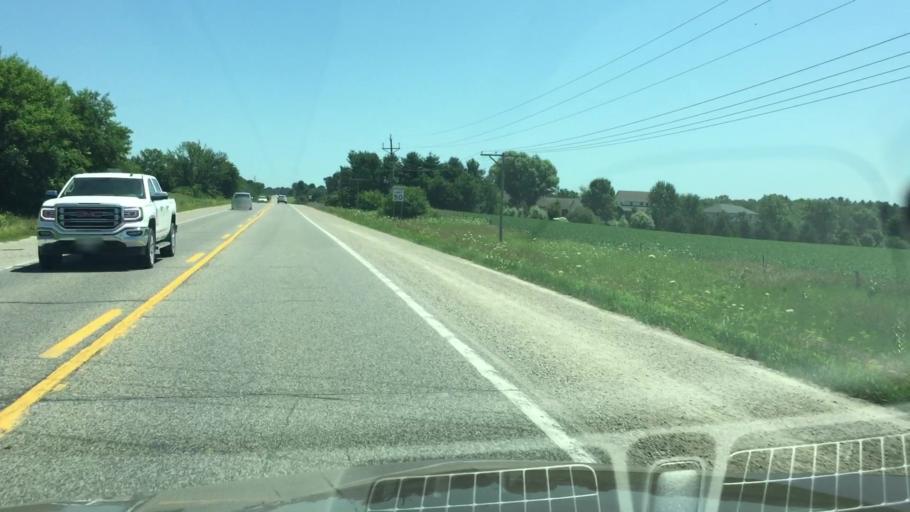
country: US
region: Iowa
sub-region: Linn County
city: Mount Vernon
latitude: 41.9161
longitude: -91.4185
